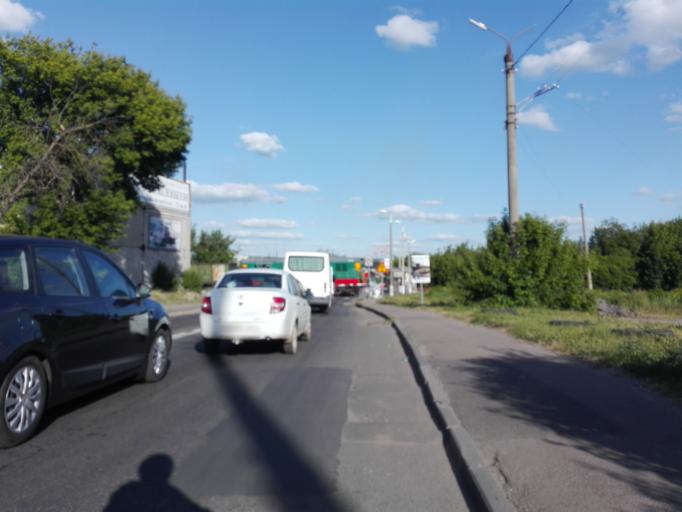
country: RU
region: Orjol
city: Orel
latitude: 52.9384
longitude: 36.0533
